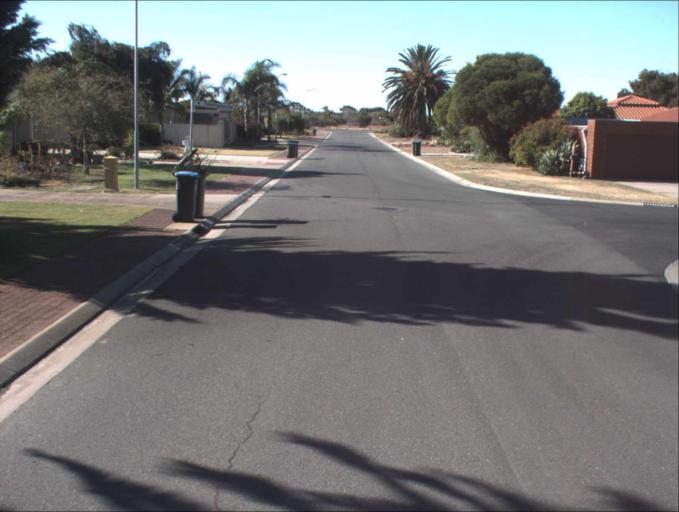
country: AU
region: South Australia
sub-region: Port Adelaide Enfield
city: Birkenhead
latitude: -34.7842
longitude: 138.4967
